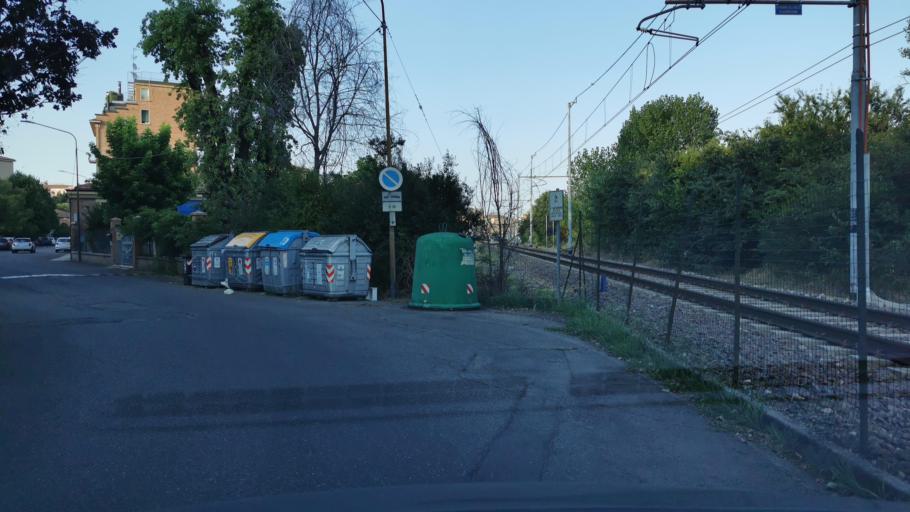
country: IT
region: Emilia-Romagna
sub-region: Provincia di Modena
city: Modena
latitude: 44.6331
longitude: 10.9266
